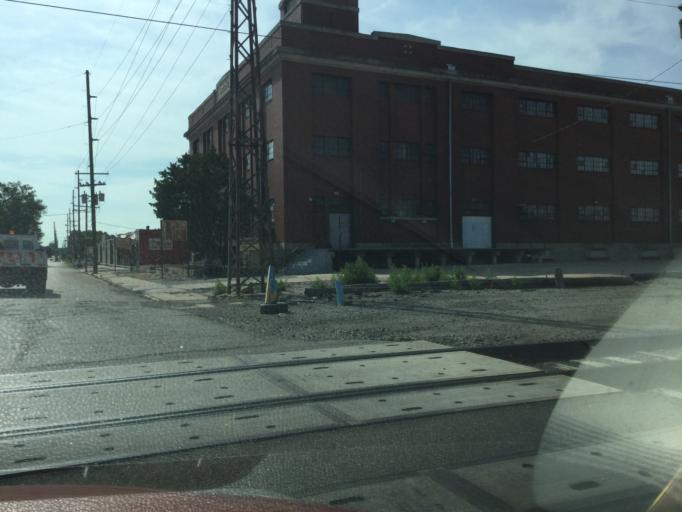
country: US
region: Kansas
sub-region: Shawnee County
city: Topeka
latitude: 39.0523
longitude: -95.6635
